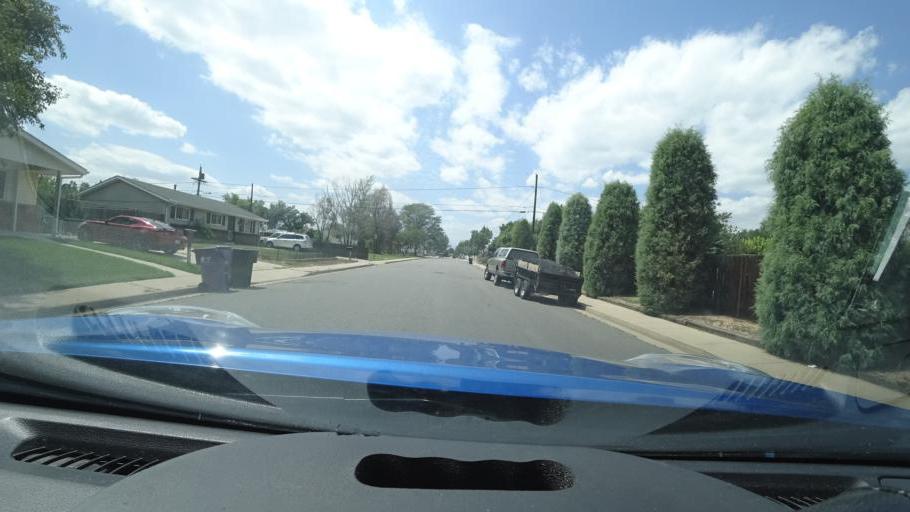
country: US
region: Colorado
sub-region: Arapahoe County
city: Sheridan
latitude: 39.6805
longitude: -105.0187
